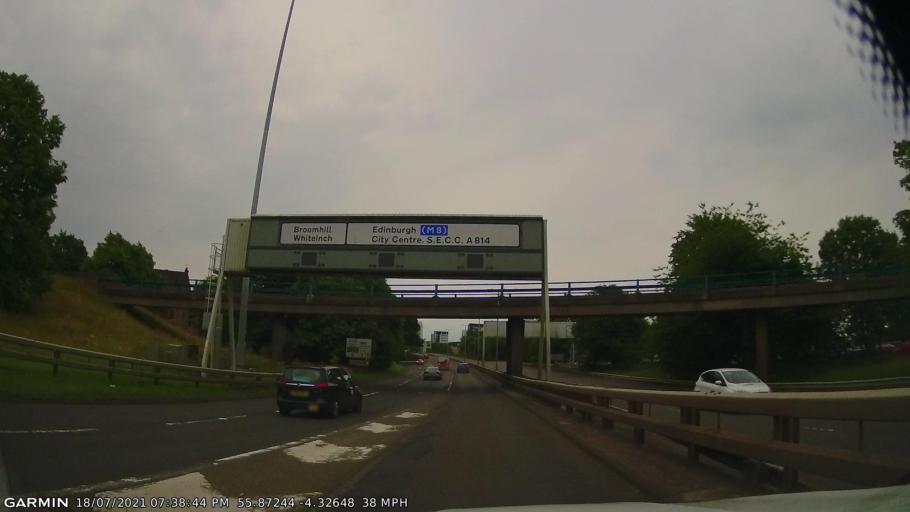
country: GB
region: Scotland
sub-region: East Dunbartonshire
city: Bearsden
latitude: 55.8724
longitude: -4.3265
